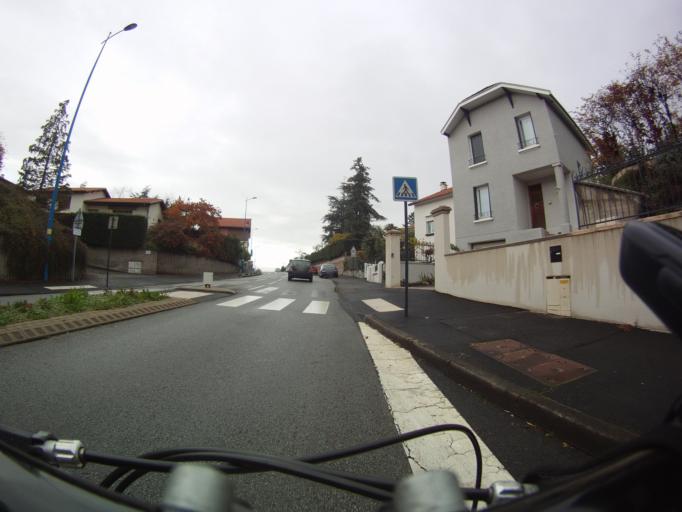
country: FR
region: Auvergne
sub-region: Departement du Puy-de-Dome
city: Aubiere
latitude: 45.7543
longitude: 3.1047
